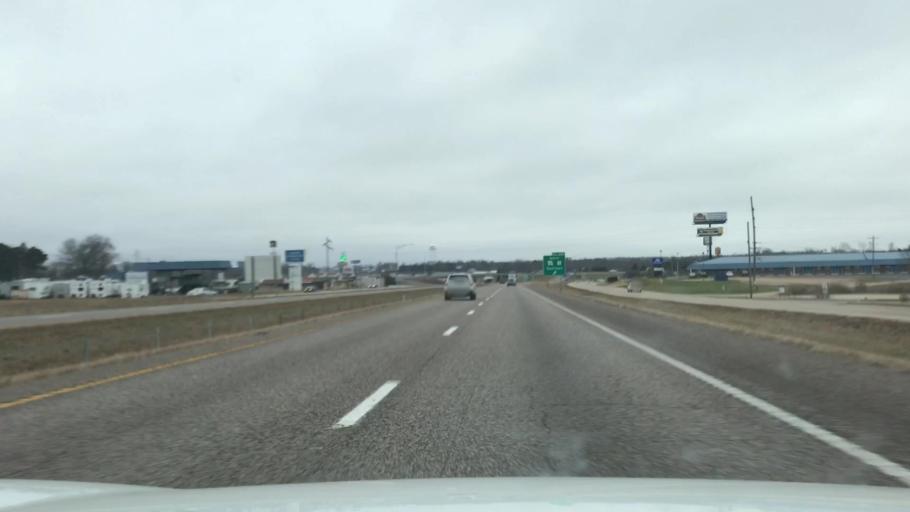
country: US
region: Missouri
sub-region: Franklin County
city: Sullivan
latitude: 38.2160
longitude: -91.1672
